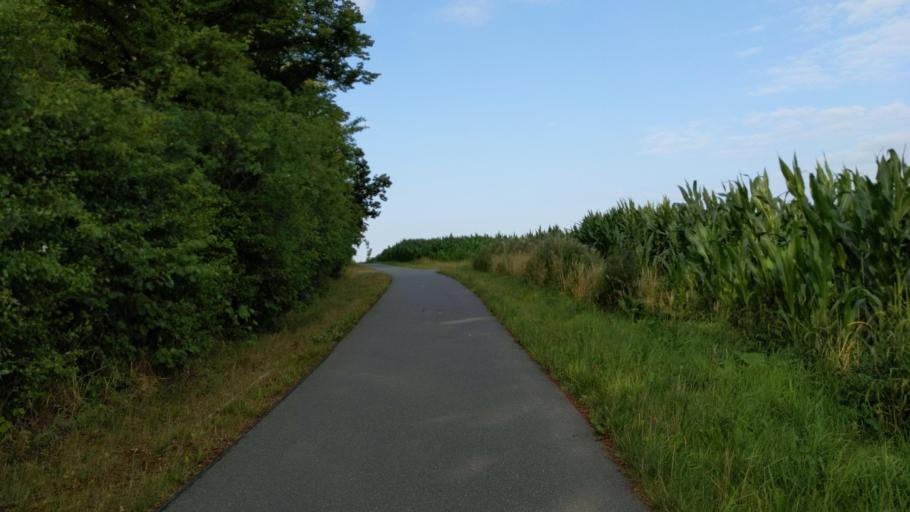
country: DE
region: Mecklenburg-Vorpommern
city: Dassow
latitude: 53.8990
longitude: 10.9366
